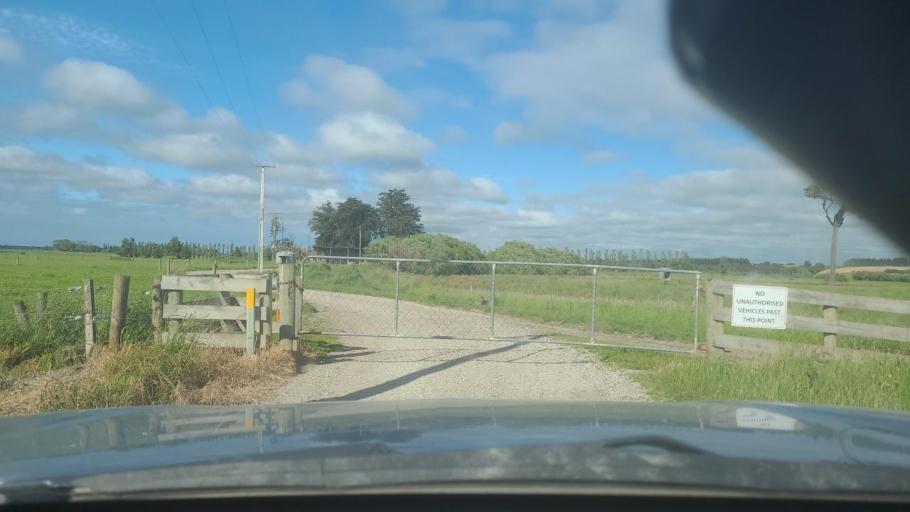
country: NZ
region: Southland
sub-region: Gore District
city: Gore
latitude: -46.4608
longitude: 168.7557
